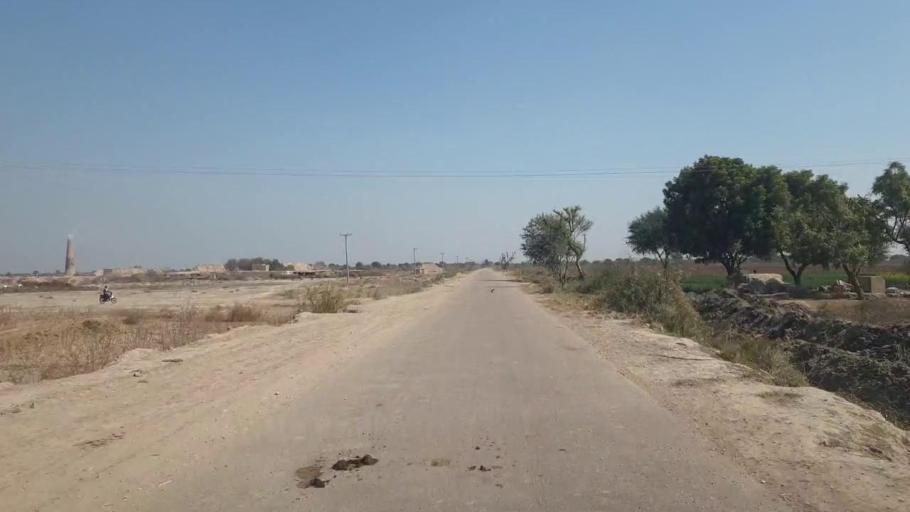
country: PK
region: Sindh
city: Chambar
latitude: 25.2886
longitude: 68.6643
